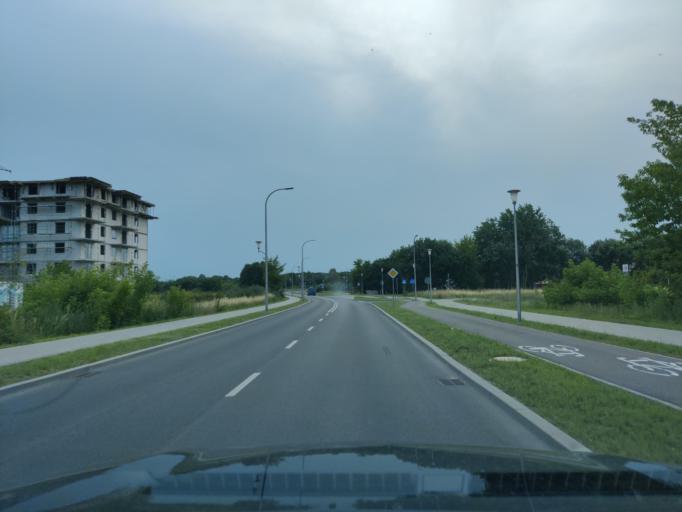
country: PL
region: Masovian Voivodeship
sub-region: Powiat mlawski
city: Mlawa
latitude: 53.1033
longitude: 20.3731
